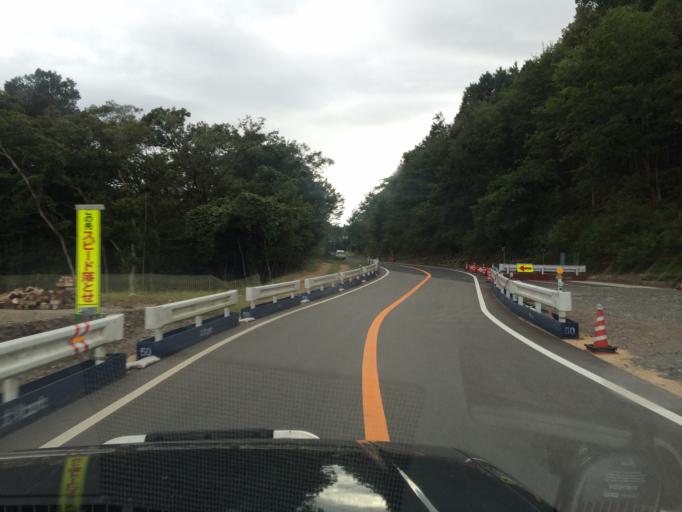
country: JP
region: Hyogo
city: Toyooka
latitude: 35.5081
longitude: 134.8022
